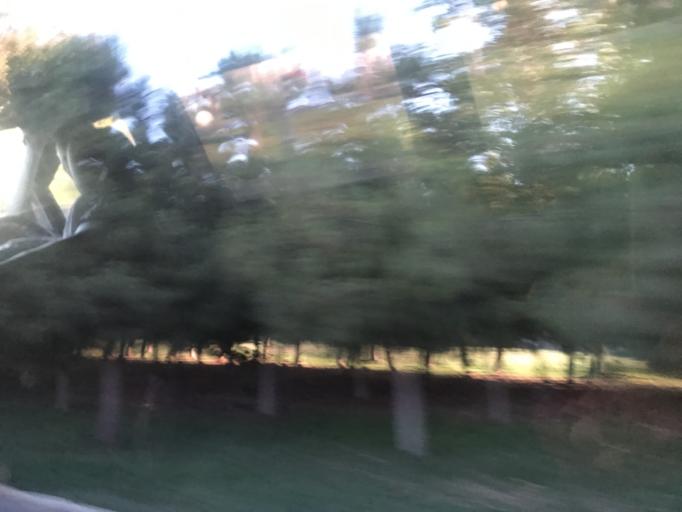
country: TR
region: Antalya
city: Antalya
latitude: 36.9314
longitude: 30.6599
